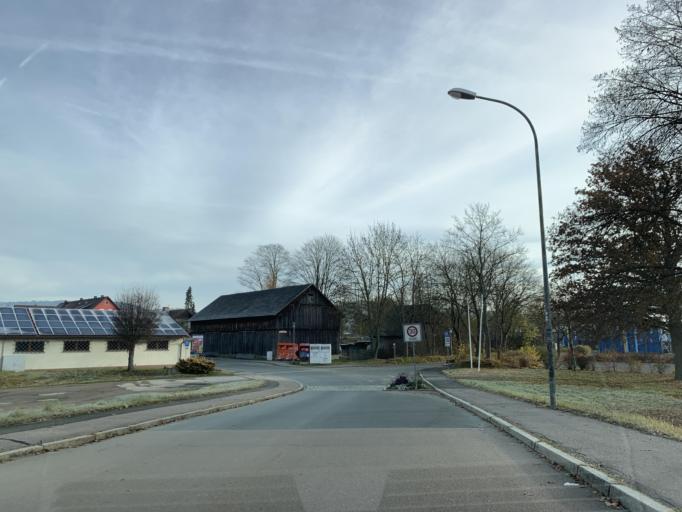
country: DE
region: Bavaria
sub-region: Upper Palatinate
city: Neunburg vorm Wald
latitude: 49.3515
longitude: 12.3830
